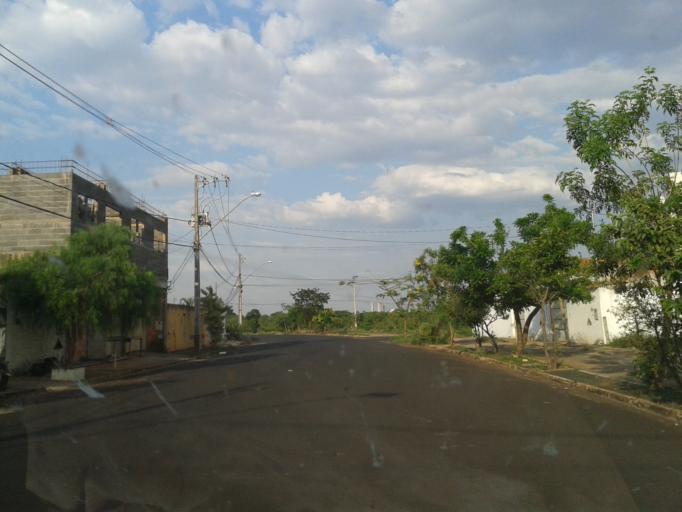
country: BR
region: Minas Gerais
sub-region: Uberlandia
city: Uberlandia
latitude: -18.9664
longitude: -48.3134
